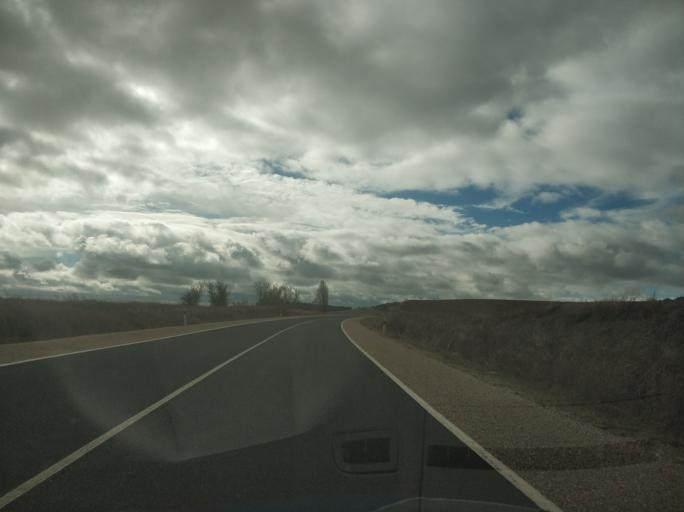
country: ES
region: Castille and Leon
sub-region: Provincia de Zamora
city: Castrillo de la Guarena
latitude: 41.2095
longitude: -5.3227
